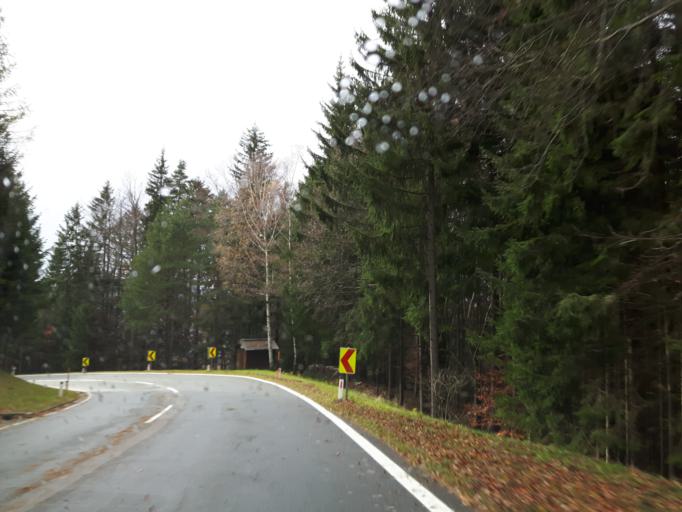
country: AT
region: Carinthia
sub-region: Politischer Bezirk Wolfsberg
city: Lavamund
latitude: 46.6470
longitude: 14.9850
